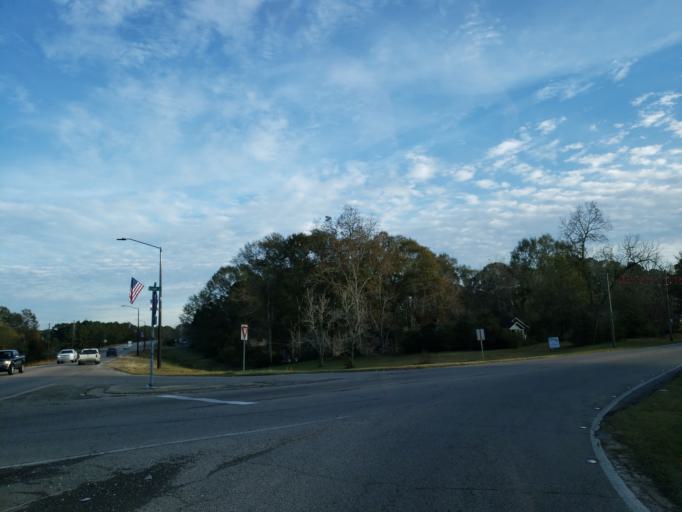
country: US
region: Mississippi
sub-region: Lamar County
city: Purvis
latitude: 31.1531
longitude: -89.4118
